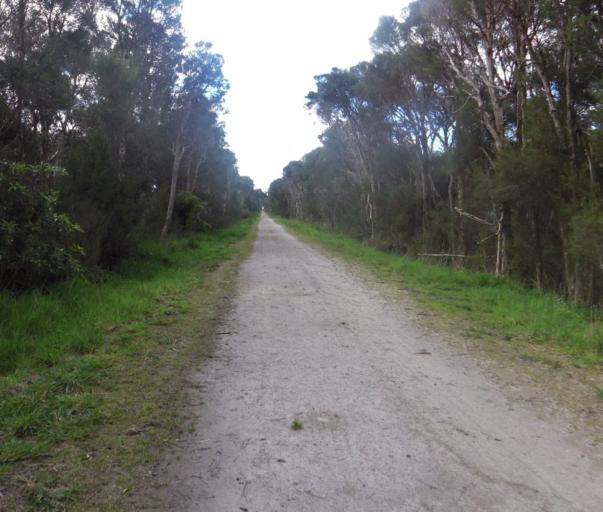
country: AU
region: Victoria
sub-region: Bass Coast
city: North Wonthaggi
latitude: -38.6389
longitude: 146.0336
